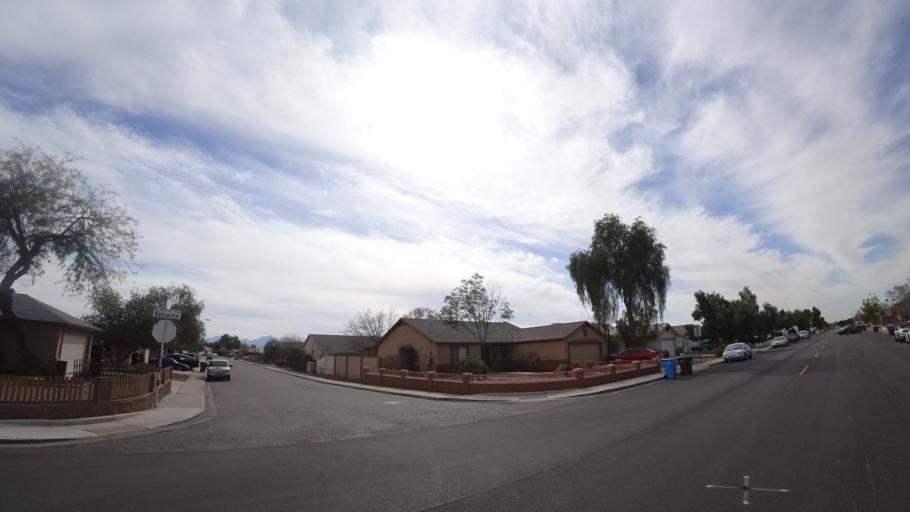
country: US
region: Arizona
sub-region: Maricopa County
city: Tolleson
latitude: 33.4725
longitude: -112.2474
